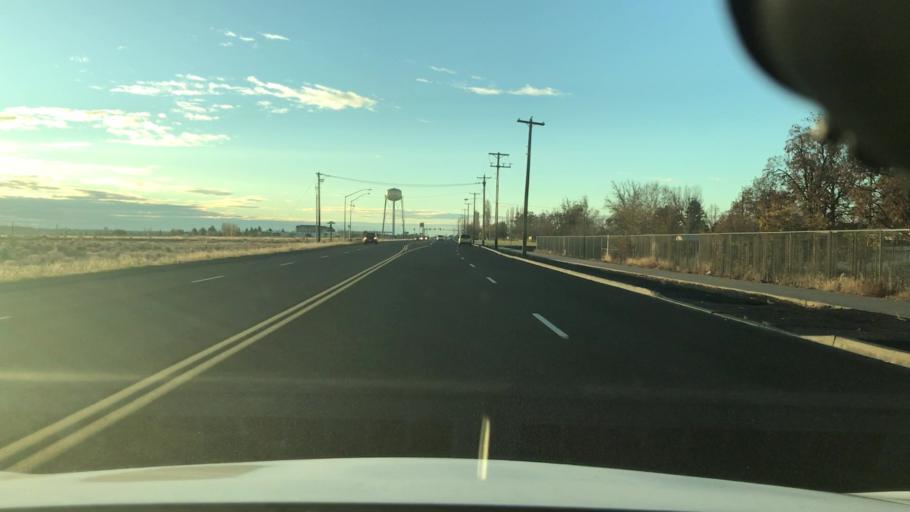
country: US
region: Washington
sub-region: Grant County
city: Moses Lake North
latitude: 47.1685
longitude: -119.3163
